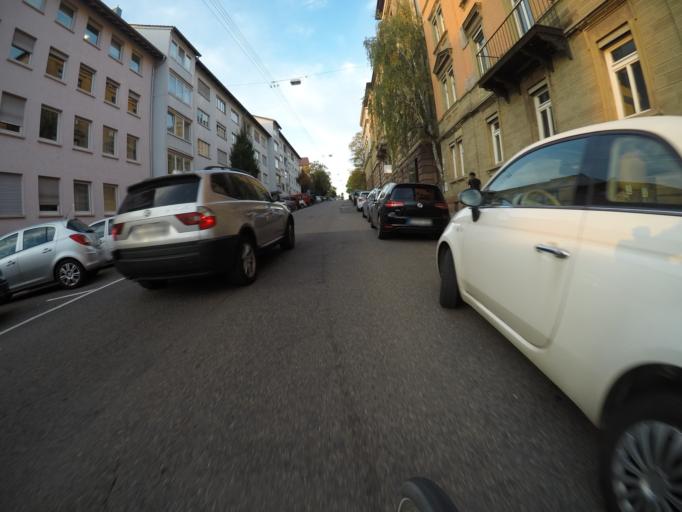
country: DE
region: Baden-Wuerttemberg
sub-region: Regierungsbezirk Stuttgart
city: Stuttgart
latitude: 48.7776
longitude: 9.1883
